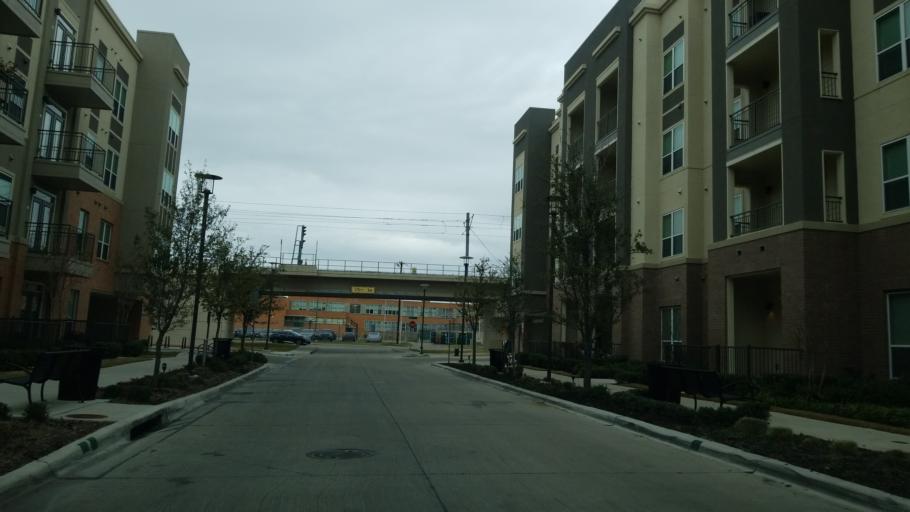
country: US
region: Texas
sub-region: Dallas County
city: University Park
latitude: 32.8239
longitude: -96.8352
